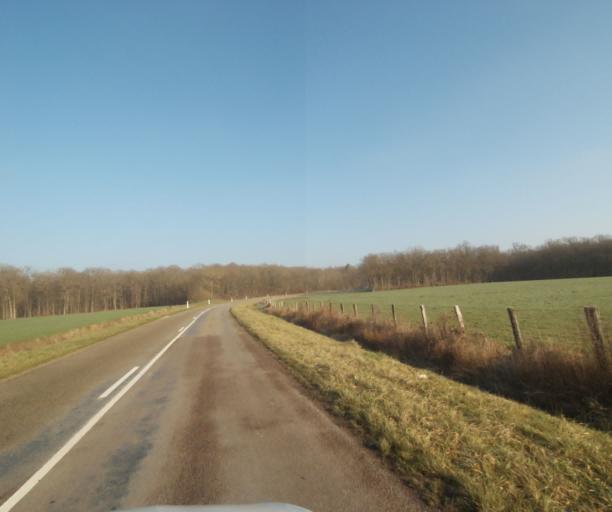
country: FR
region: Champagne-Ardenne
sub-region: Departement de la Haute-Marne
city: Montier-en-Der
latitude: 48.4775
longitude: 4.7871
